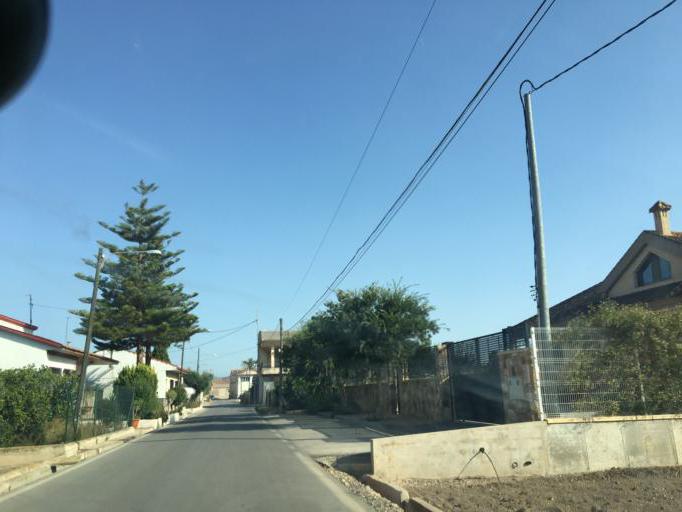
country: ES
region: Murcia
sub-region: Murcia
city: Santomera
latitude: 38.0298
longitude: -1.0671
